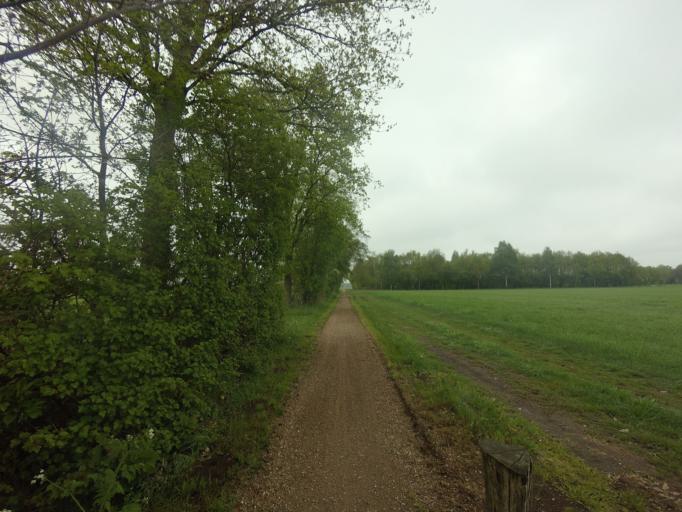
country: NL
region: Overijssel
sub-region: Gemeente Haaksbergen
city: Haaksbergen
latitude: 52.1307
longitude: 6.8095
